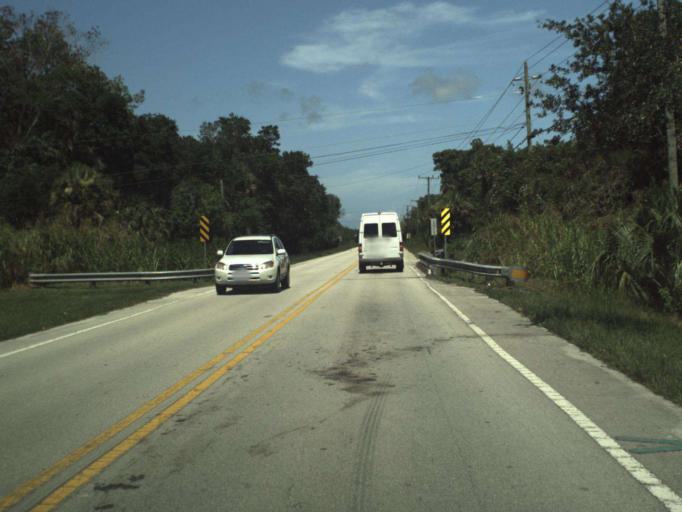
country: US
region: Florida
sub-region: Indian River County
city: Sebastian
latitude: 27.7487
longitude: -80.4872
